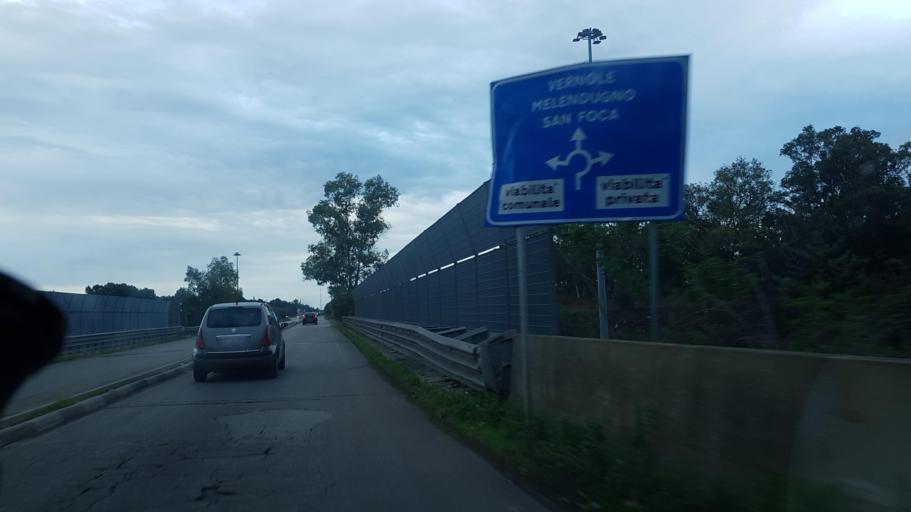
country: IT
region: Apulia
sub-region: Provincia di Lecce
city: Merine
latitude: 40.3444
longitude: 18.2029
